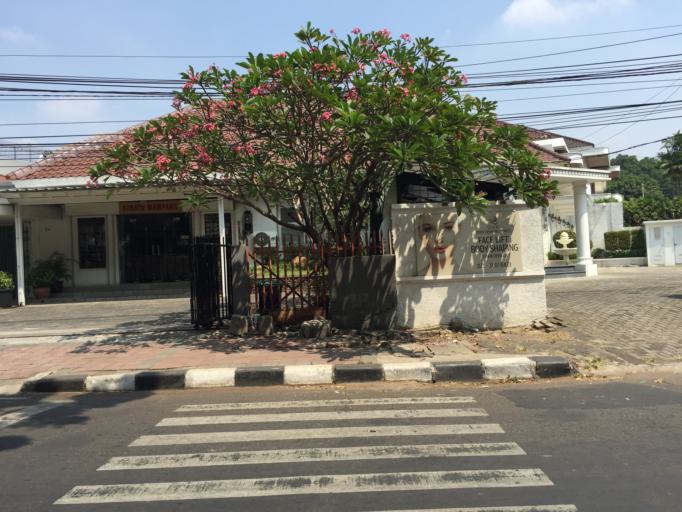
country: ID
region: Jakarta Raya
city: Jakarta
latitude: -6.1999
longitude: 106.8374
